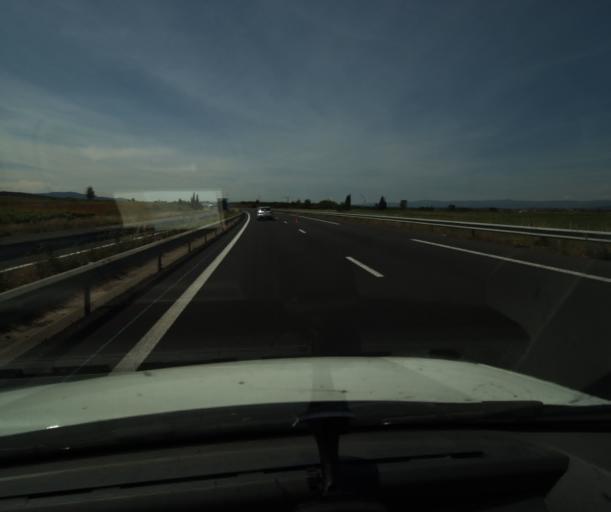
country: FR
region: Languedoc-Roussillon
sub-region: Departement de l'Aude
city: Ornaisons
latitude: 43.1662
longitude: 2.8364
